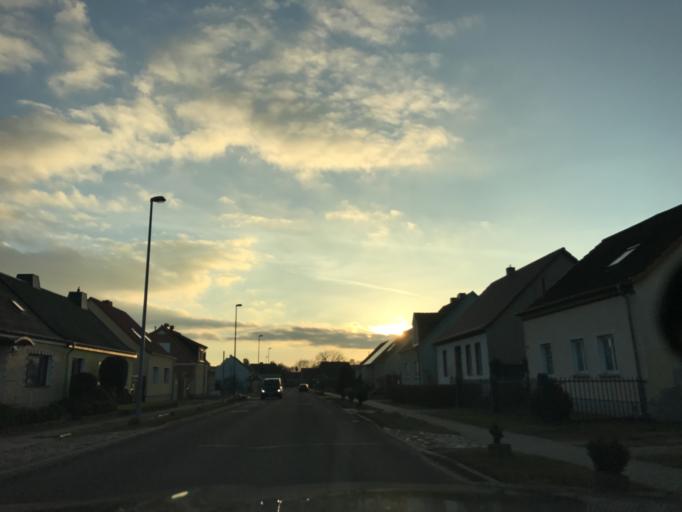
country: DE
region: Brandenburg
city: Wusterwitz
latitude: 52.4086
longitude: 12.3750
